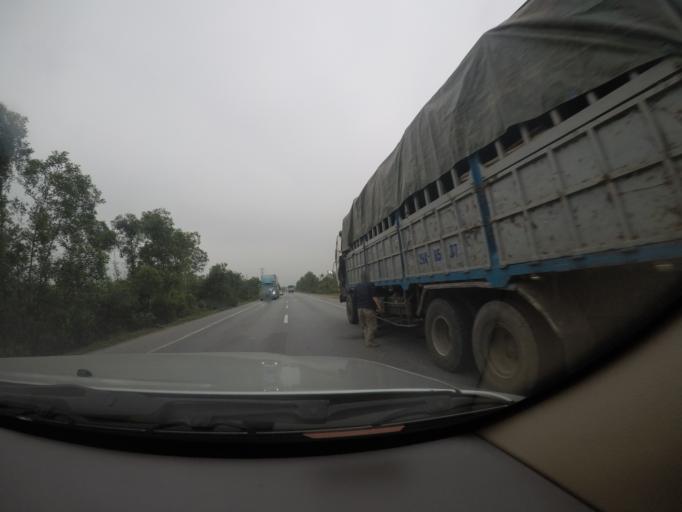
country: VN
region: Ha Tinh
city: Ky Anh
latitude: 18.0281
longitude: 106.3360
